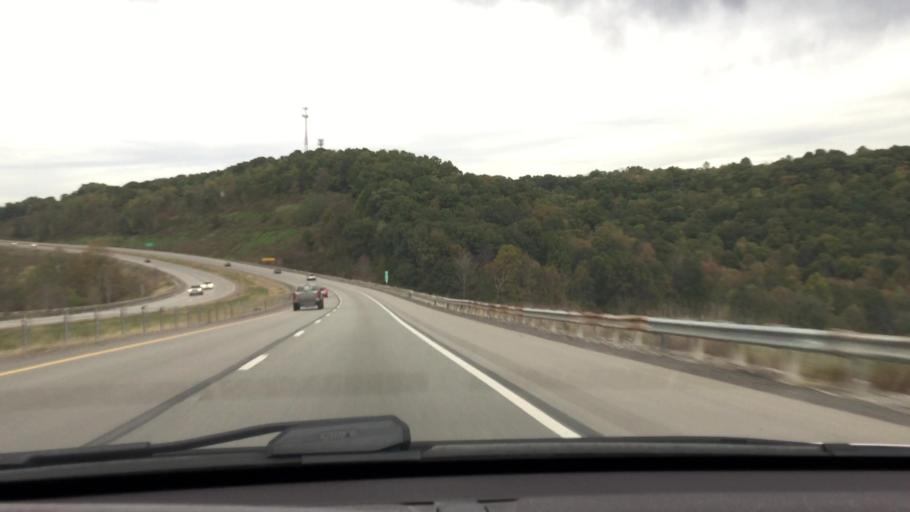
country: US
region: Pennsylvania
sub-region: Beaver County
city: West Mayfield
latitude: 40.7443
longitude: -80.3672
